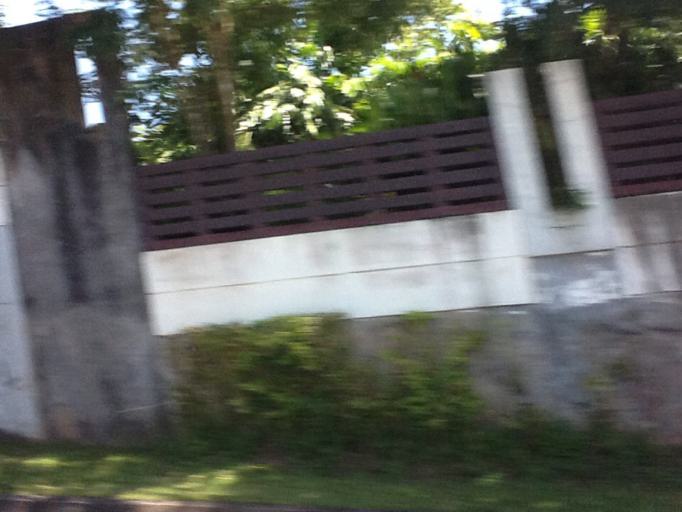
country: TH
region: Phuket
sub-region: Amphoe Kathu
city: Kathu
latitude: 7.9333
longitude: 98.3331
